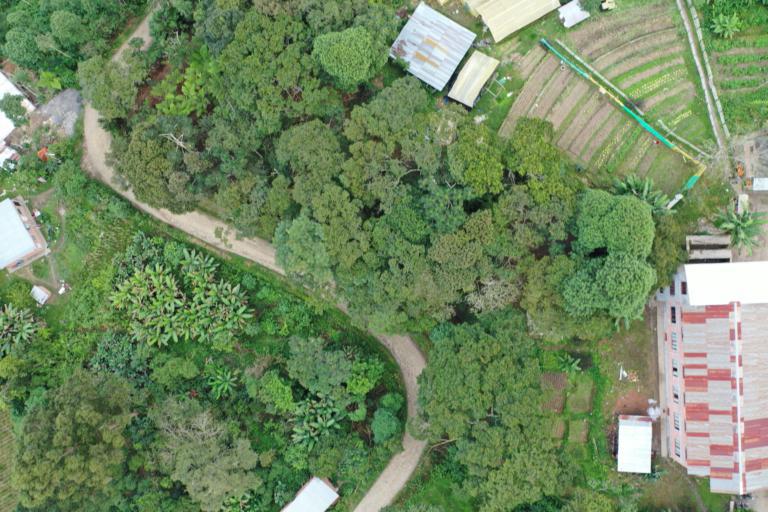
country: BO
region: La Paz
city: Coroico
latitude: -16.2590
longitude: -67.6911
